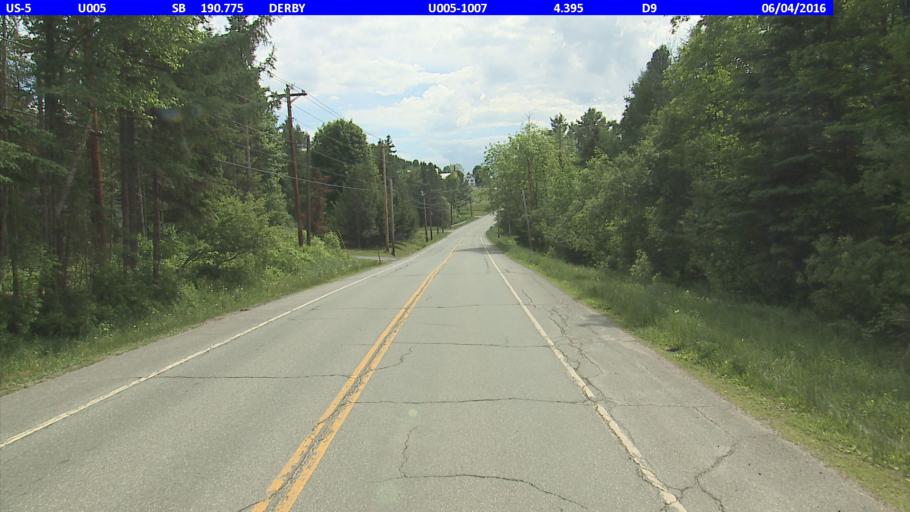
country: US
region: Vermont
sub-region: Orleans County
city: Newport
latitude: 44.9846
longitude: -72.1076
